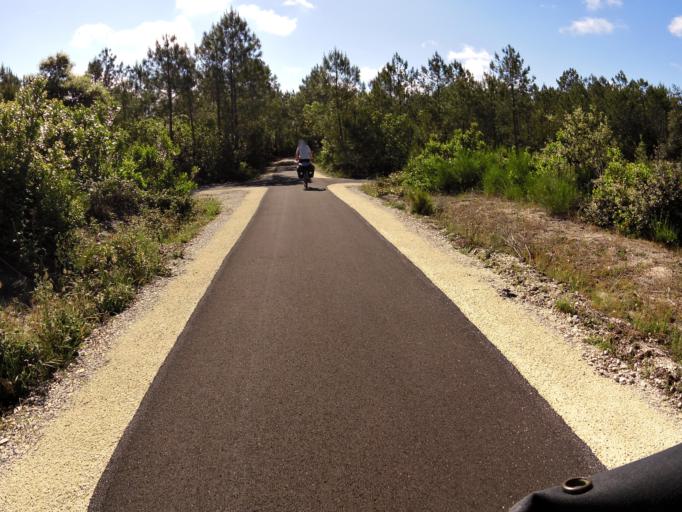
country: FR
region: Aquitaine
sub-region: Departement de la Gironde
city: Lacanau
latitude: 45.0321
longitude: -1.1775
